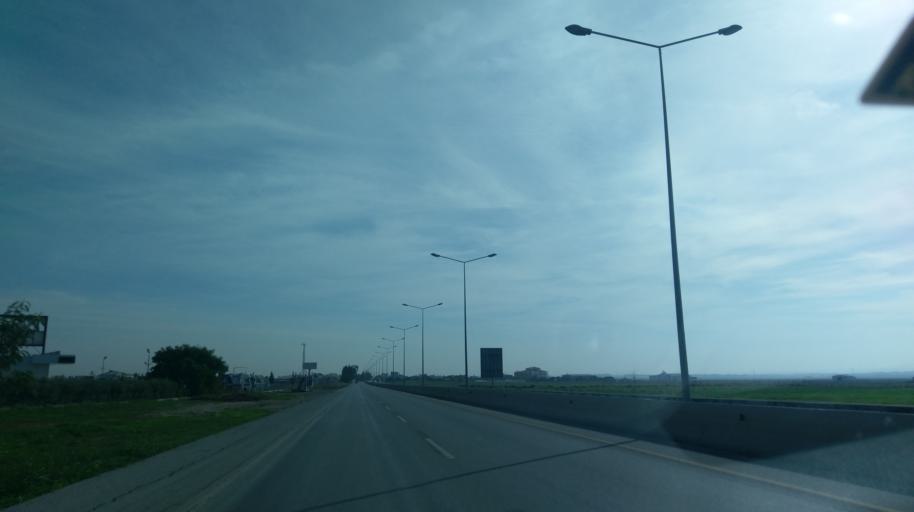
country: CY
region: Lefkosia
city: Geri
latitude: 35.2176
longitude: 33.5031
